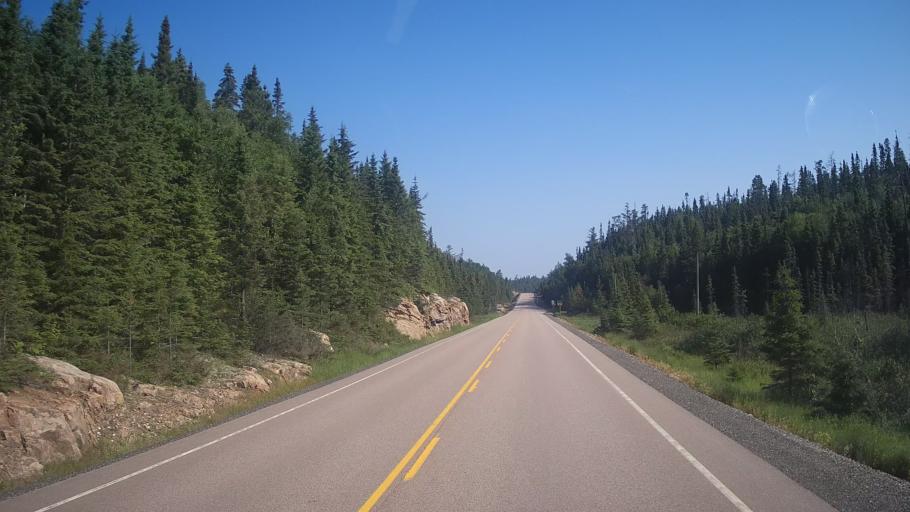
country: CA
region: Ontario
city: Rayside-Balfour
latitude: 47.0020
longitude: -81.6327
